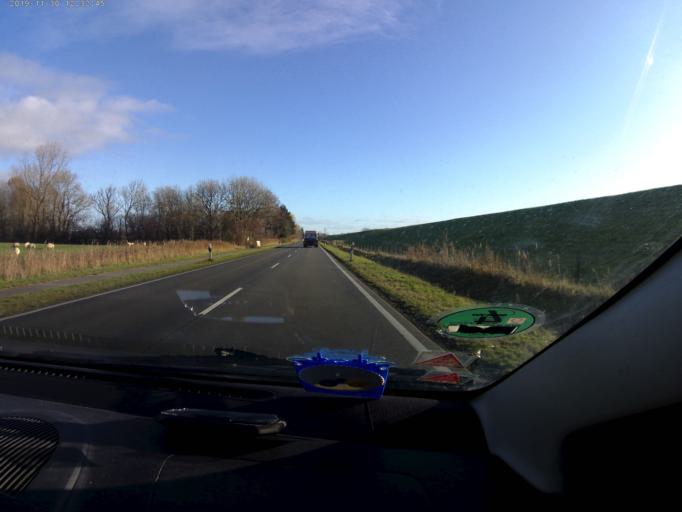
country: DE
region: Lower Saxony
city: Jemgum
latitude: 53.2340
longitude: 7.4146
